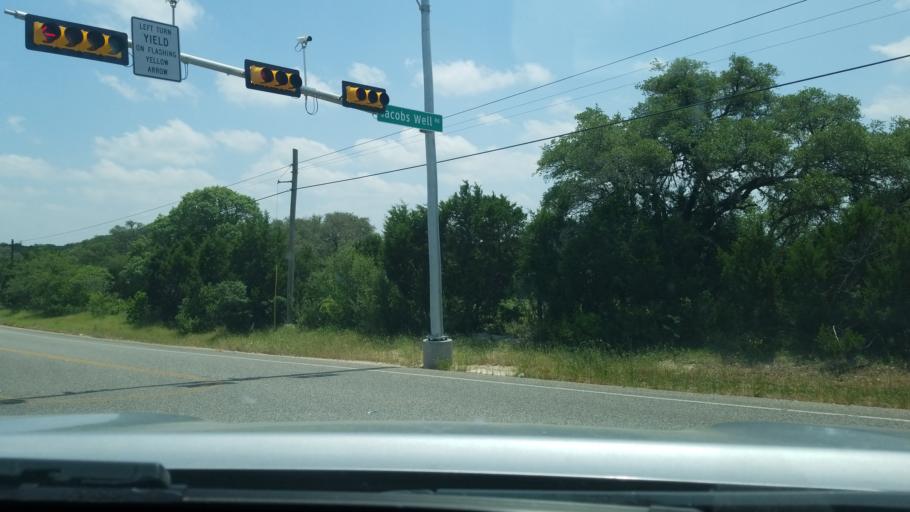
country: US
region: Texas
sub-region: Hays County
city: Woodcreek
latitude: 30.0194
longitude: -98.1305
